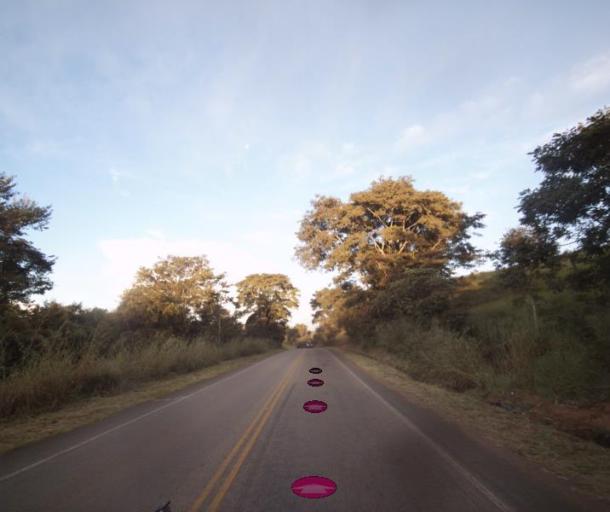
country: BR
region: Goias
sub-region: Abadiania
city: Abadiania
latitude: -16.1106
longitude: -48.8813
